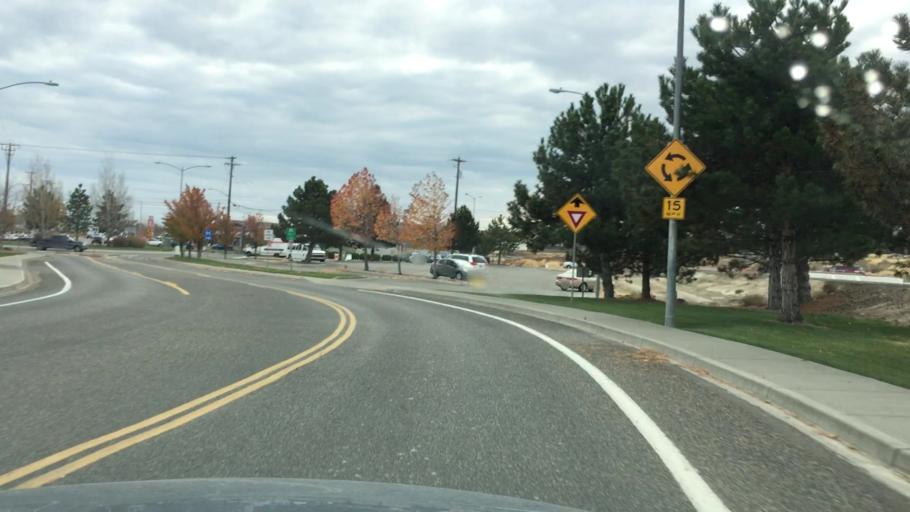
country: US
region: Washington
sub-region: Benton County
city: Kennewick
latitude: 46.1850
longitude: -119.1821
